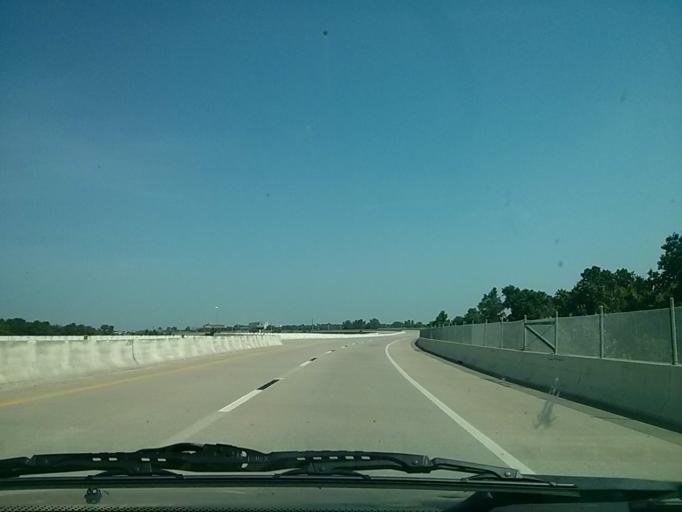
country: US
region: Oklahoma
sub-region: Tulsa County
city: Broken Arrow
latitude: 36.0178
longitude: -95.8486
